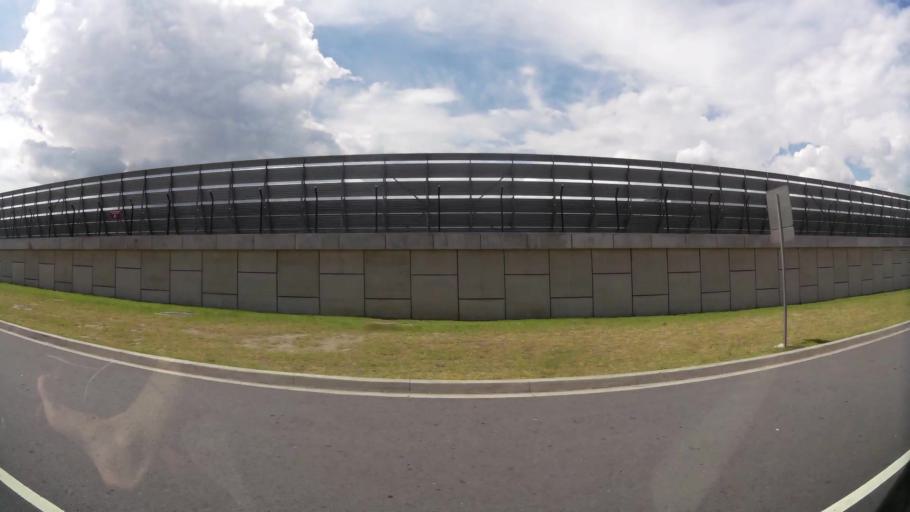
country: EC
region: Pichincha
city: Quito
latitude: -0.1347
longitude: -78.3585
